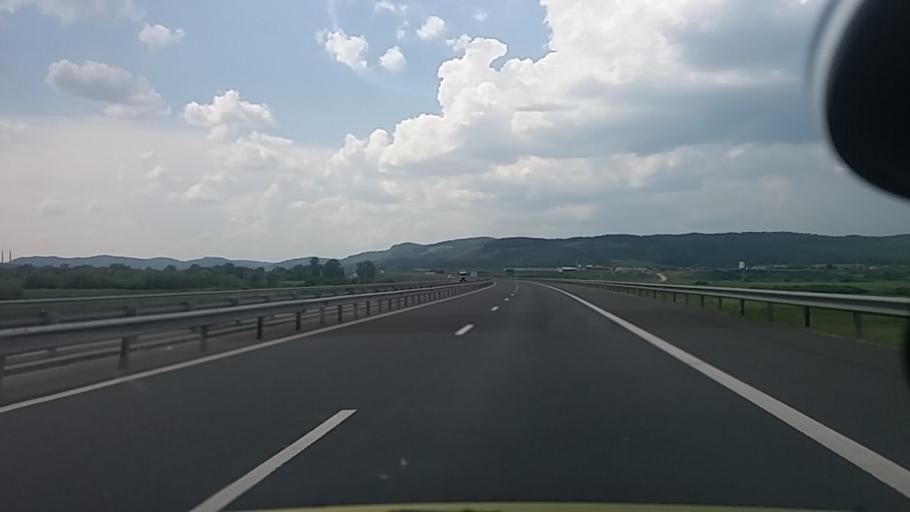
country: RO
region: Hunedoara
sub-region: Comuna Harau
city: Harau
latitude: 45.9032
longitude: 22.9275
